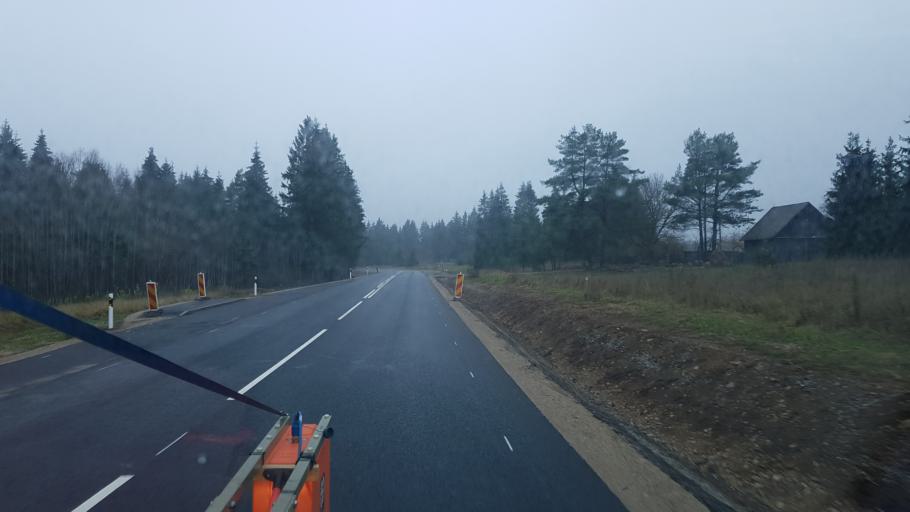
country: EE
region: Raplamaa
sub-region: Kohila vald
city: Kohila
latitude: 59.1774
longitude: 24.8272
